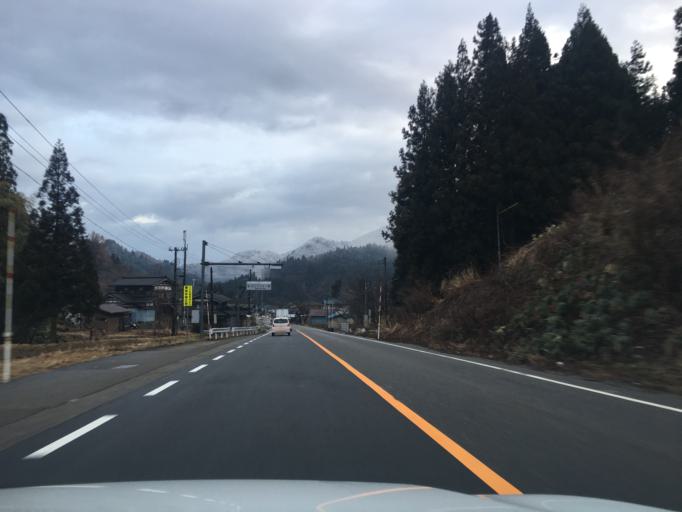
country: JP
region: Niigata
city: Murakami
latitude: 38.3849
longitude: 139.5542
